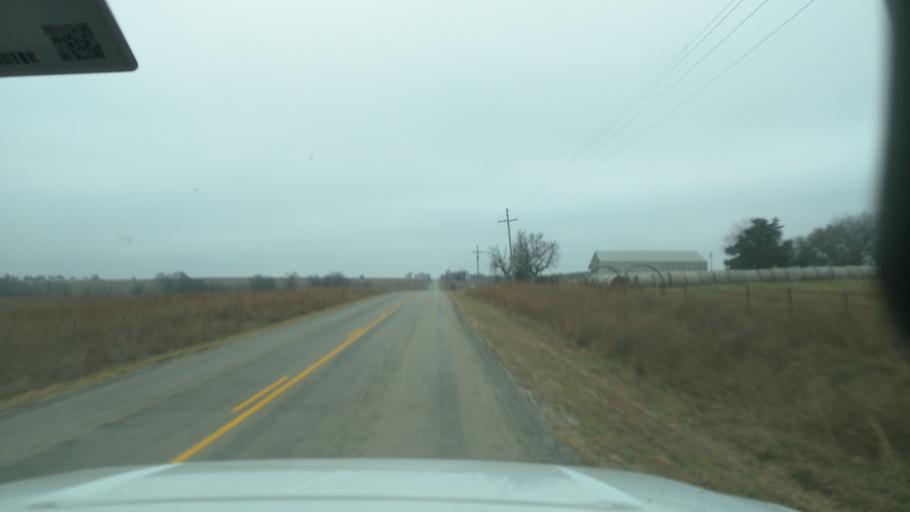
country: US
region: Kansas
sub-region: Lyon County
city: Emporia
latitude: 38.5905
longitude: -96.2610
